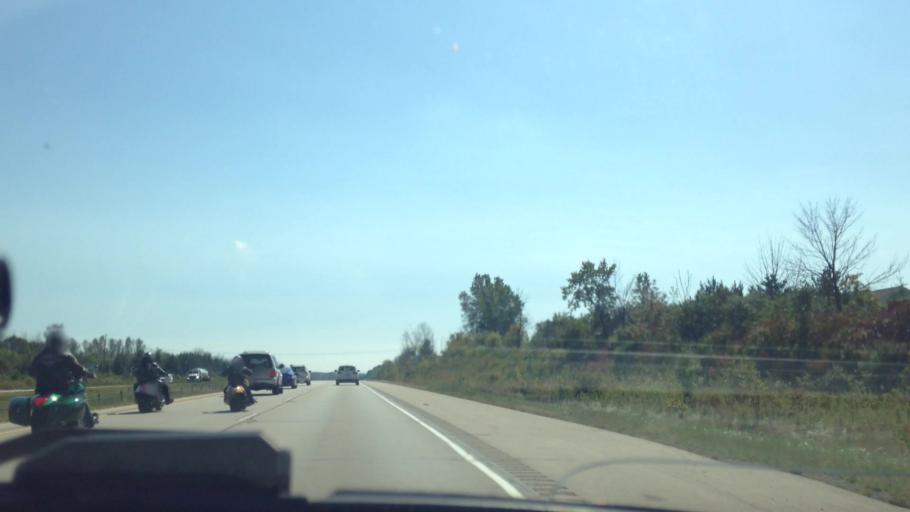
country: US
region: Wisconsin
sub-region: Ozaukee County
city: Thiensville
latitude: 43.2456
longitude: -87.9201
